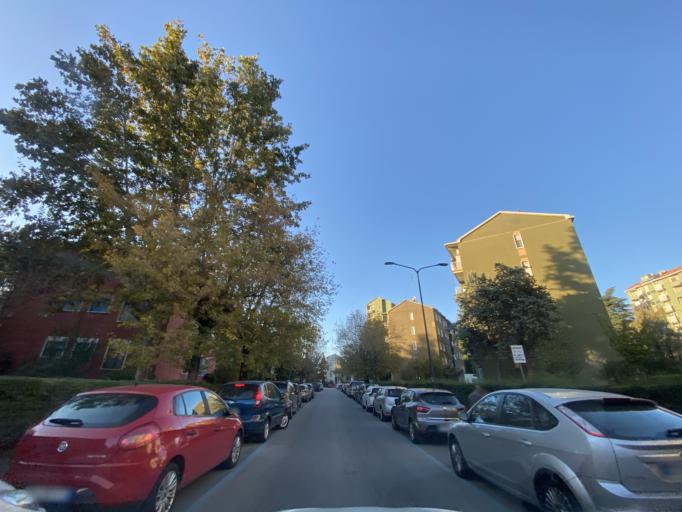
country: IT
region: Lombardy
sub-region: Citta metropolitana di Milano
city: Cormano
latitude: 45.5269
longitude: 9.1591
